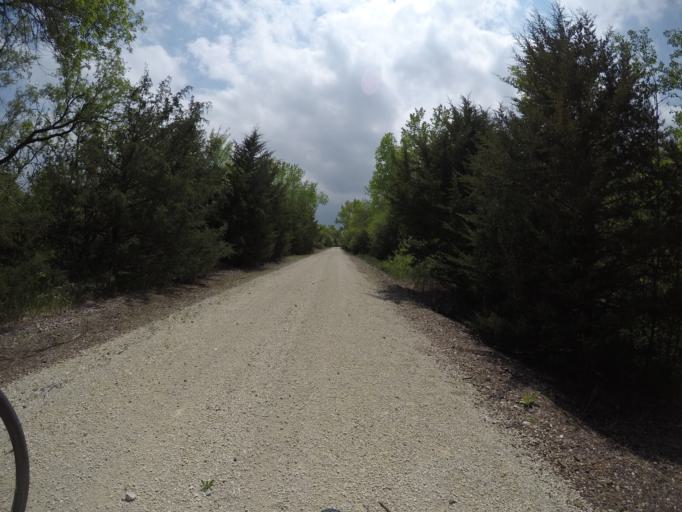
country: US
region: Nebraska
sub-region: Gage County
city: Wymore
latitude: 40.2039
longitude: -96.6606
